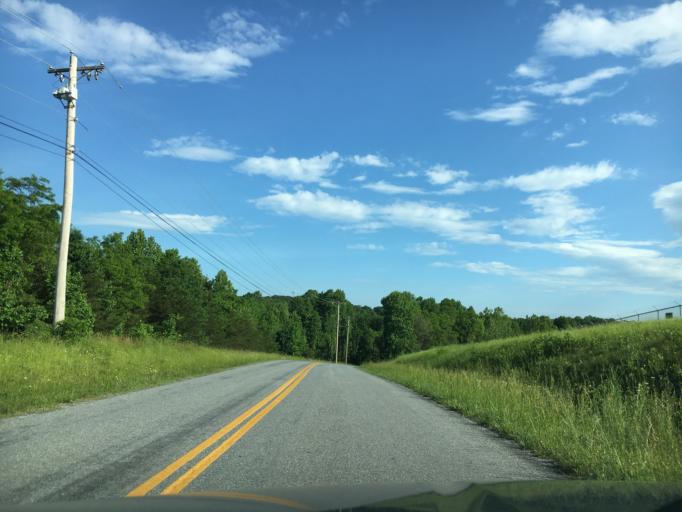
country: US
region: Virginia
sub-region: Campbell County
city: Timberlake
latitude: 37.3338
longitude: -79.2021
